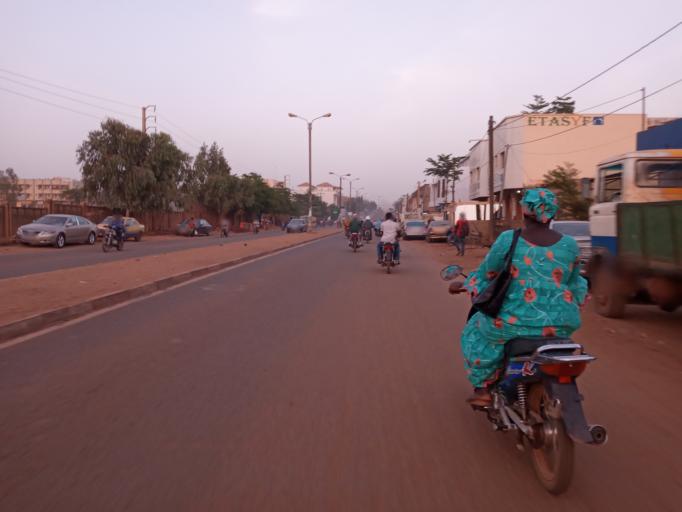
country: ML
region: Bamako
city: Bamako
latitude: 12.5757
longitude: -7.9576
